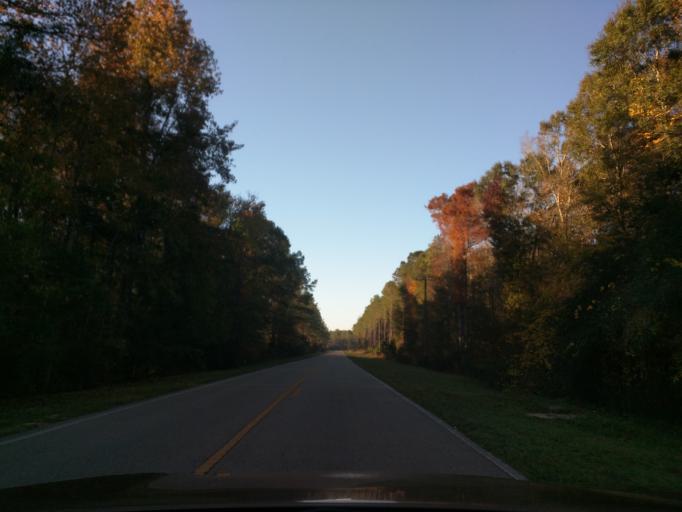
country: US
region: Florida
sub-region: Leon County
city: Woodville
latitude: 30.3259
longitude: -84.1477
